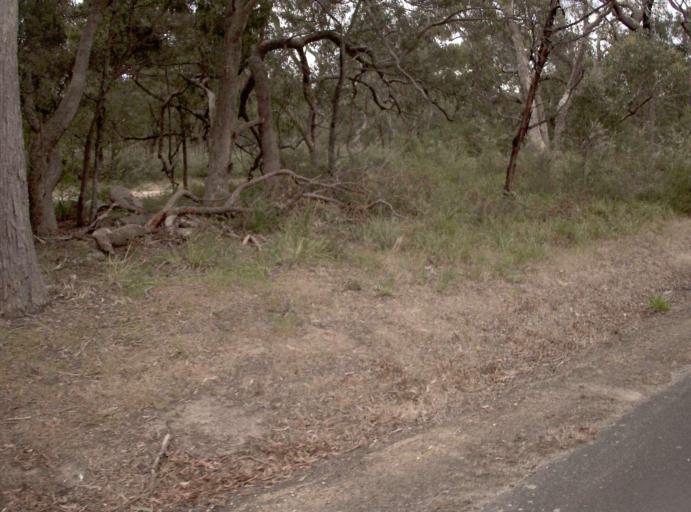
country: AU
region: Victoria
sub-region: Wellington
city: Sale
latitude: -38.2504
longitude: 147.0526
